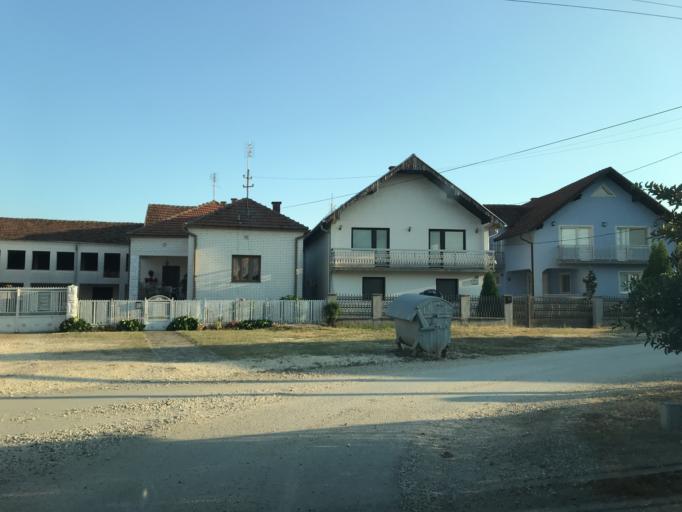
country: RO
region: Mehedinti
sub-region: Comuna Burila Mare
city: Burila Mare
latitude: 44.4925
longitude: 22.4934
